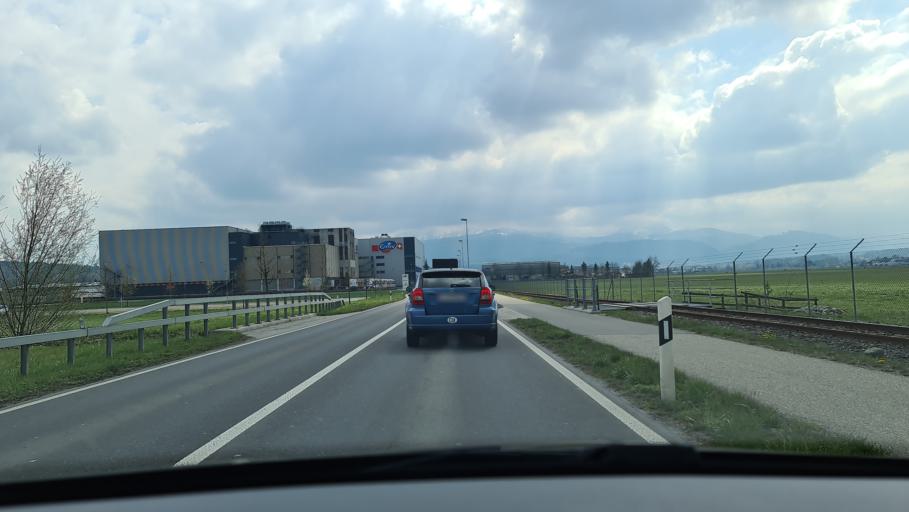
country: CH
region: Lucerne
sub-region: Lucerne-Land District
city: Ebikon
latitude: 47.0988
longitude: 8.3157
